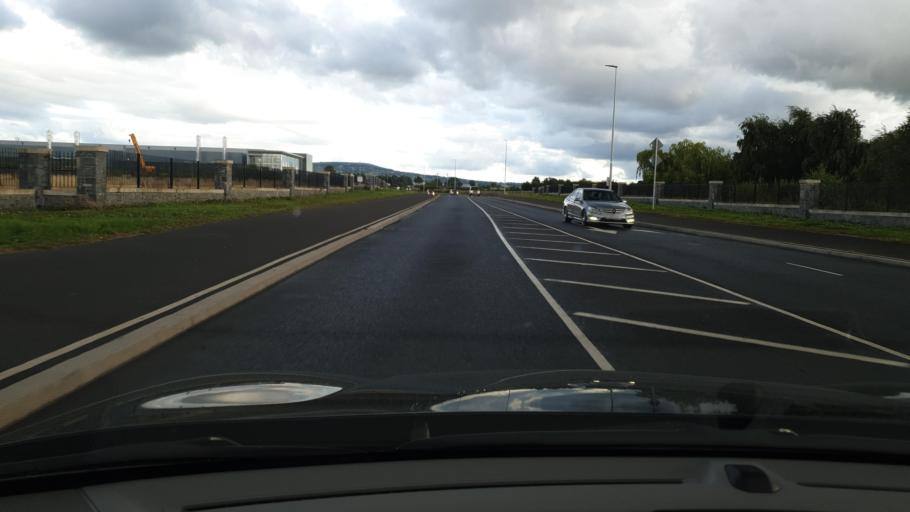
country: IE
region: Leinster
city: Lucan
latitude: 53.3203
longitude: -6.4567
